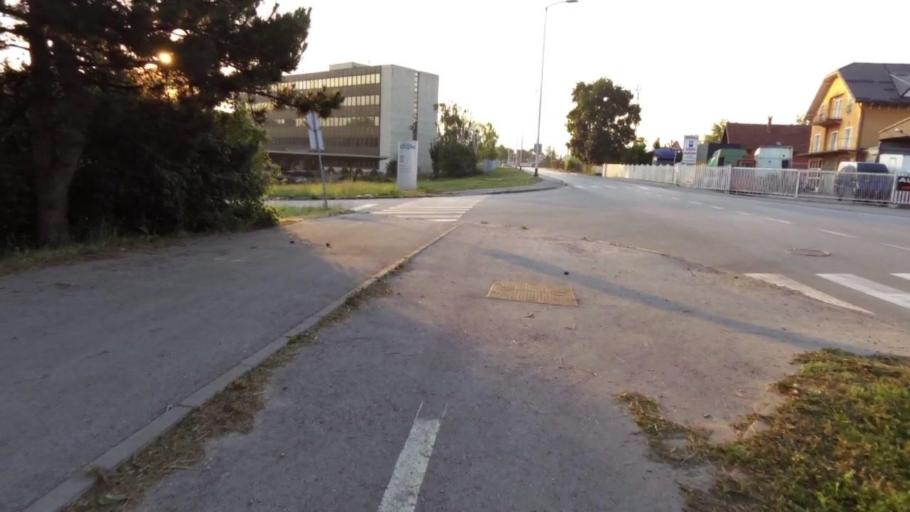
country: HR
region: Grad Zagreb
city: Dubrava
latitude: 45.8004
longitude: 16.0771
